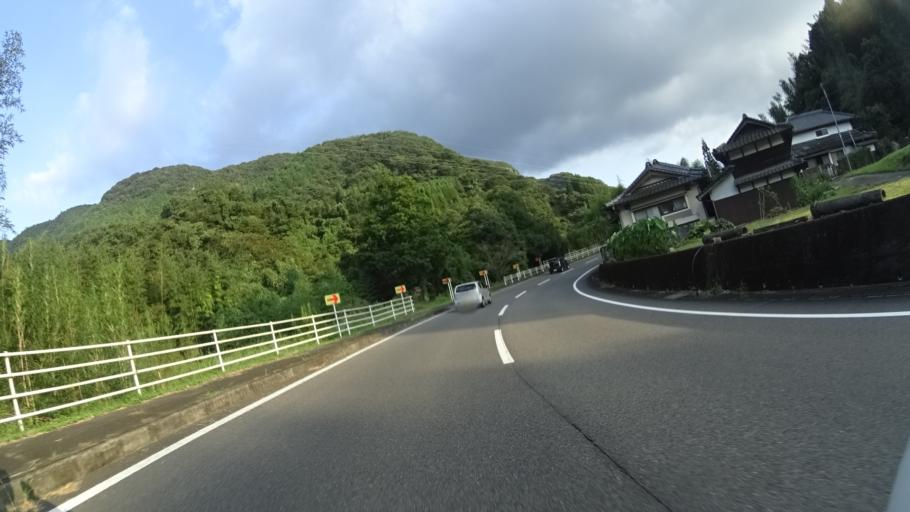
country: JP
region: Oita
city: Hiji
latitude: 33.3683
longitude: 131.3974
